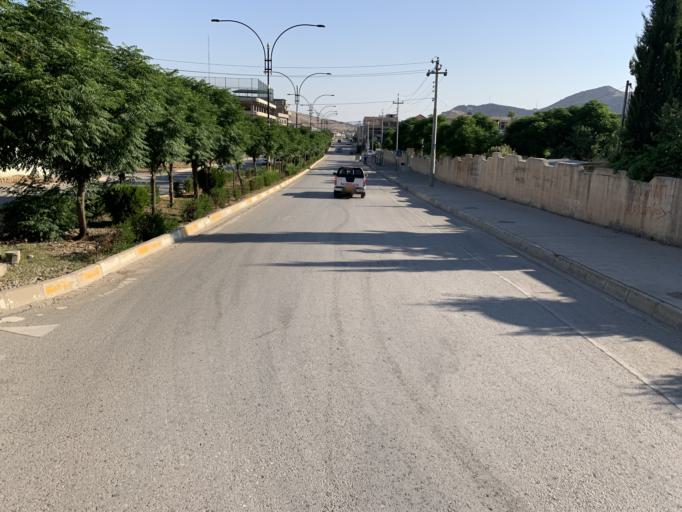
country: IQ
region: As Sulaymaniyah
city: Raniye
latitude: 36.2448
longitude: 44.8736
